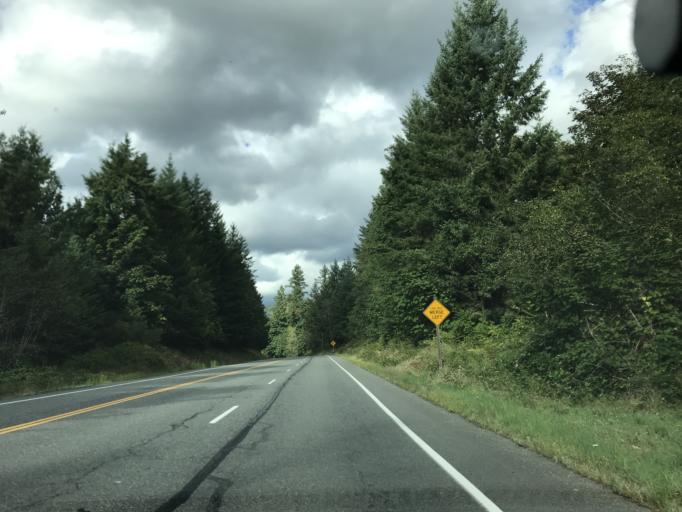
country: US
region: Washington
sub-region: King County
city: Black Diamond
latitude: 47.2952
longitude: -122.0529
